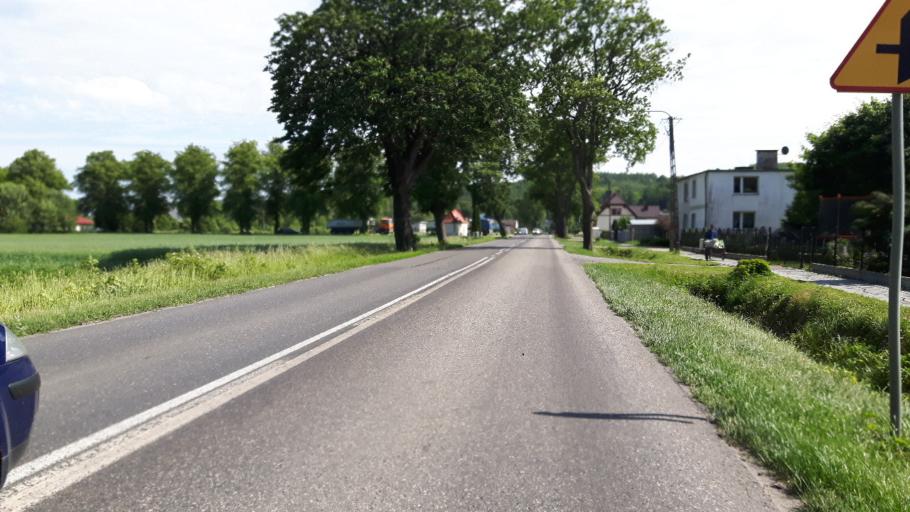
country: PL
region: Pomeranian Voivodeship
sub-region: Powiat wejherowski
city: Orle
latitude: 54.6538
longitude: 18.0991
